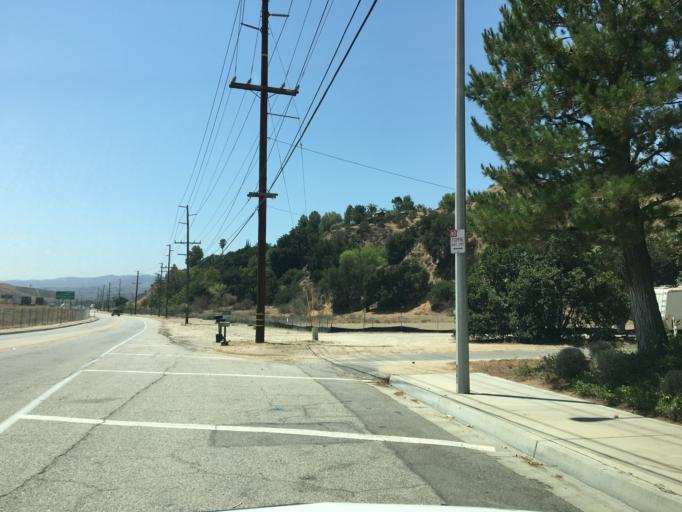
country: US
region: California
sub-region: Los Angeles County
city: Castaic
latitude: 34.4675
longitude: -118.6172
